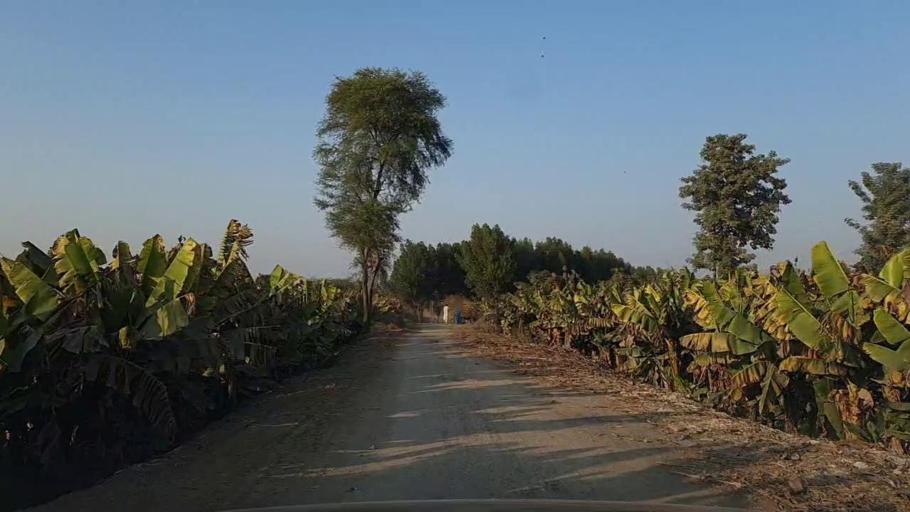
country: PK
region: Sindh
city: Daur
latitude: 26.4660
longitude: 68.3880
